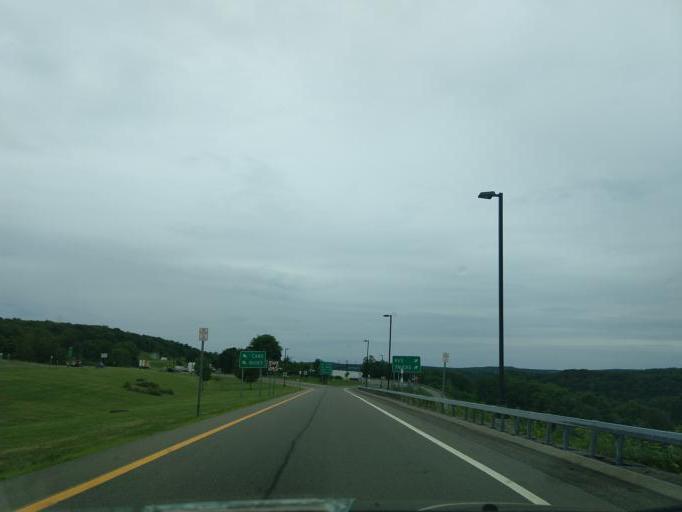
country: US
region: New York
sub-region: Chenango County
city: Lakeview
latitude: 42.3773
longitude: -75.9950
